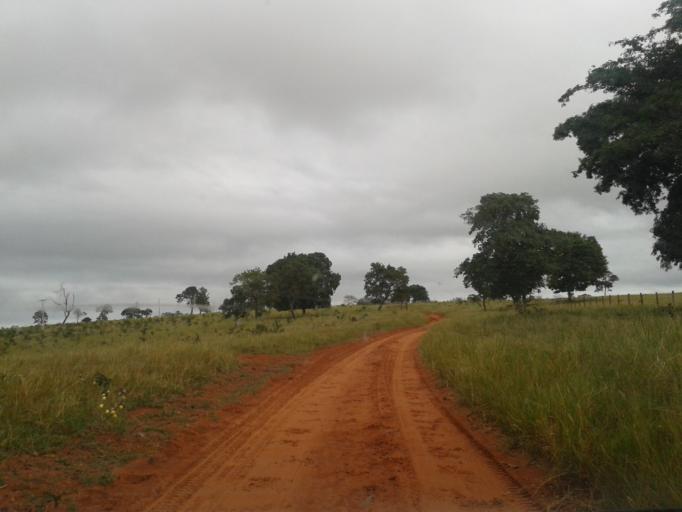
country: BR
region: Minas Gerais
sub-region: Campina Verde
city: Campina Verde
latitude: -19.4091
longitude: -49.6461
